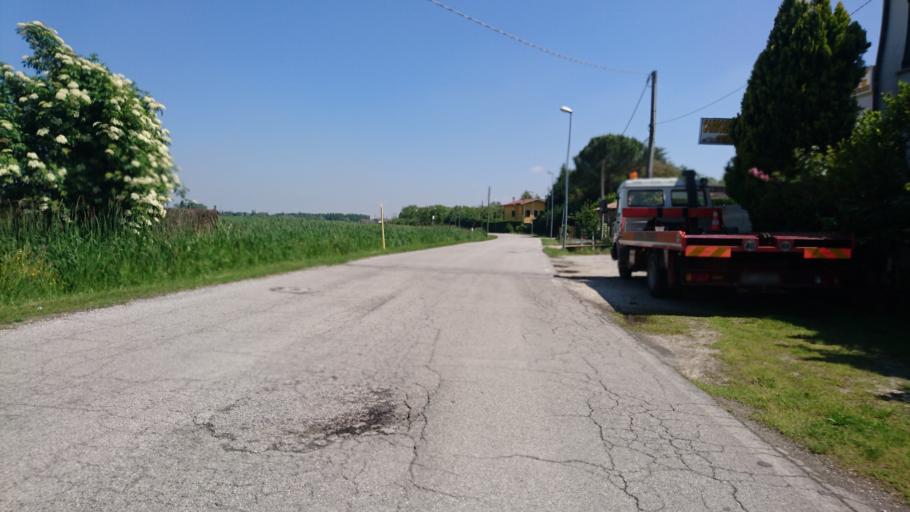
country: IT
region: Veneto
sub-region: Provincia di Padova
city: Casalserugo
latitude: 45.2969
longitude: 11.9159
